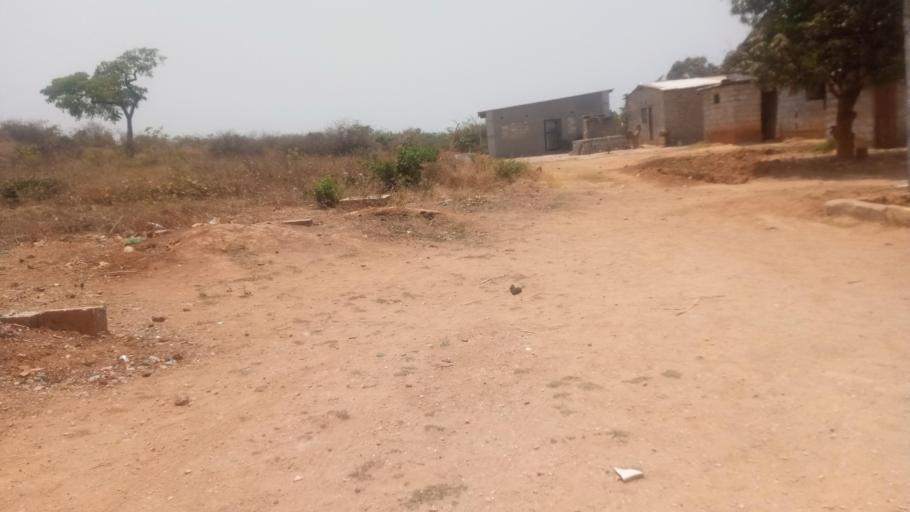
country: ZM
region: Lusaka
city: Lusaka
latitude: -15.4392
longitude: 28.3745
